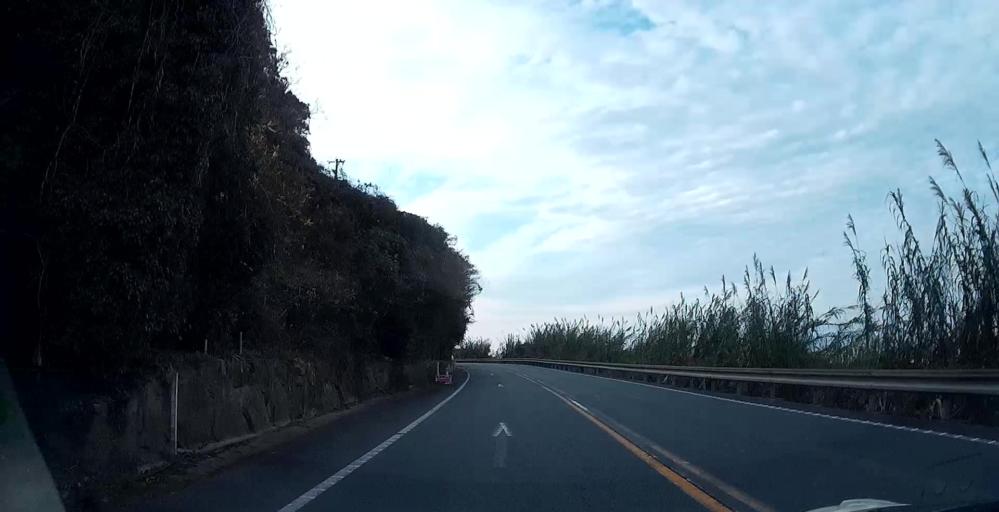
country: JP
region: Kumamoto
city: Matsubase
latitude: 32.6540
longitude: 130.5021
